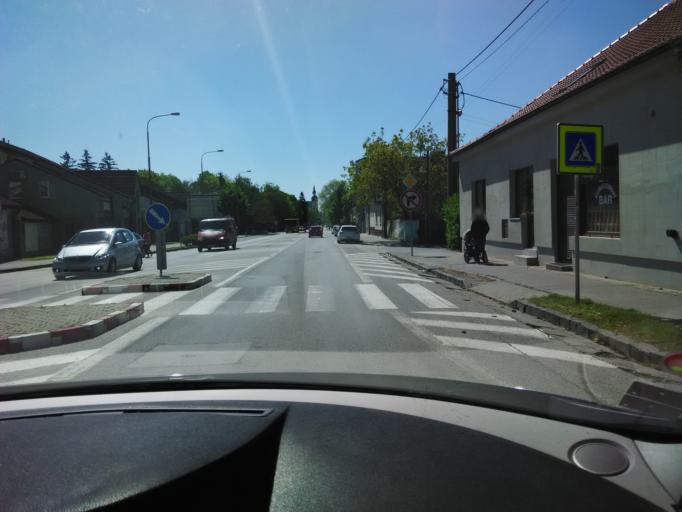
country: SK
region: Trnavsky
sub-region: Okres Trnava
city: Trnava
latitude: 48.3878
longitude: 17.5914
